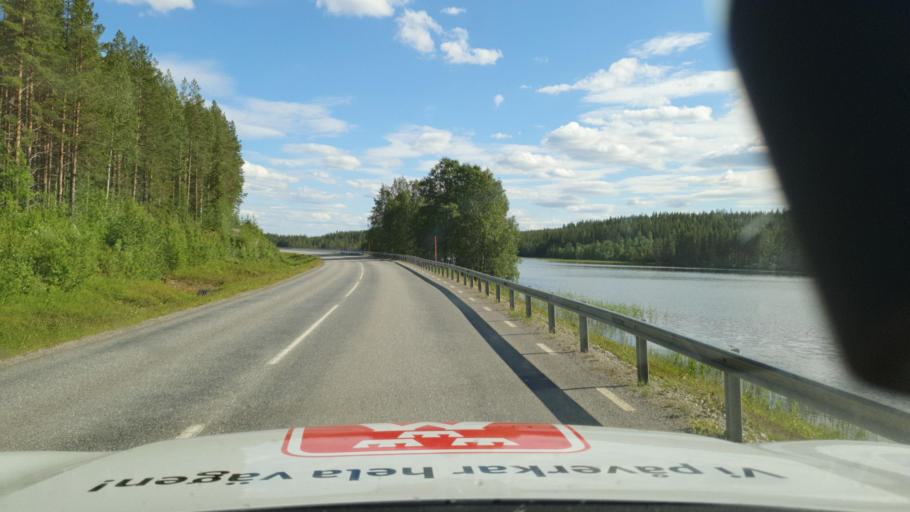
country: SE
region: Vaesterbotten
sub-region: Norsjo Kommun
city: Norsjoe
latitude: 64.8625
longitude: 19.7277
